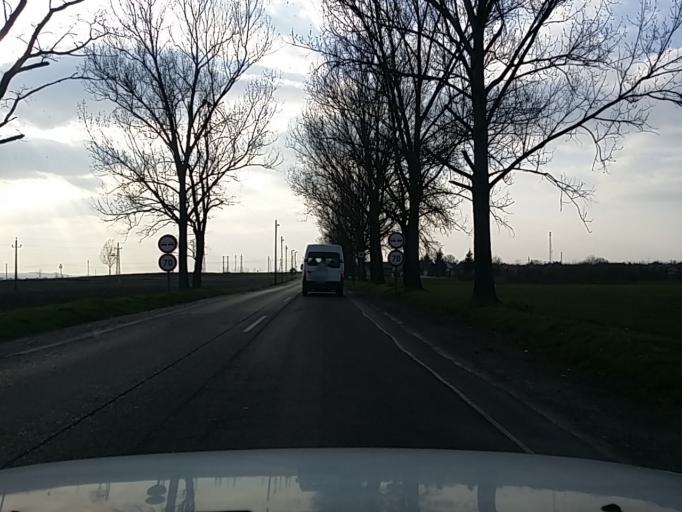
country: HU
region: Borsod-Abauj-Zemplen
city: Putnok
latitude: 48.3011
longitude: 20.3845
